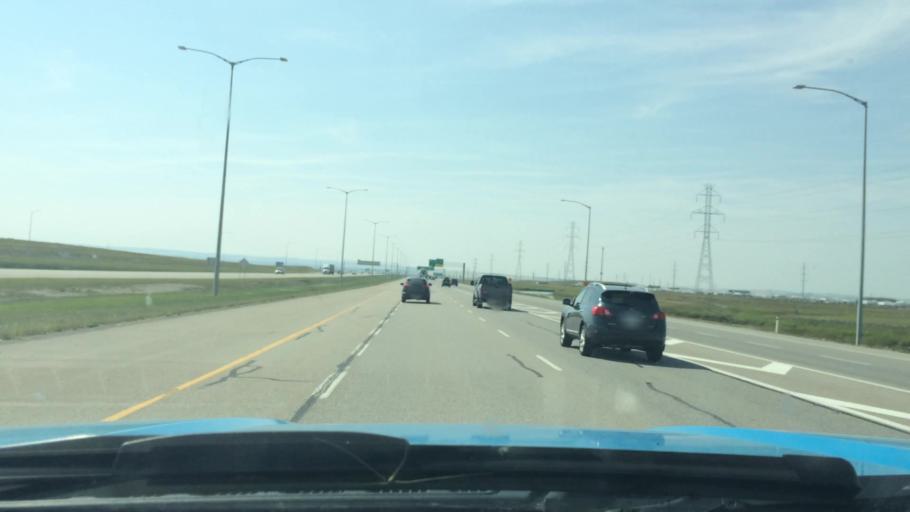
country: CA
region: Alberta
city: Airdrie
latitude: 51.1760
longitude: -113.9667
